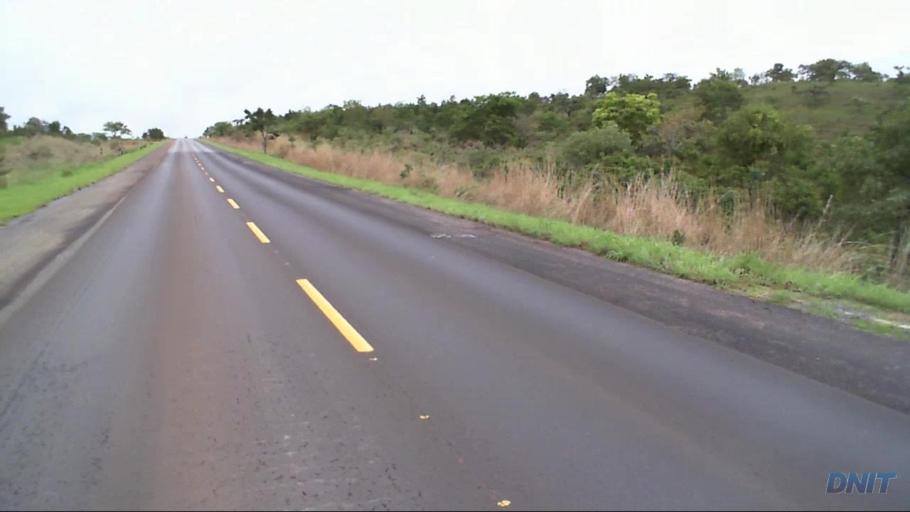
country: BR
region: Goias
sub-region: Padre Bernardo
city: Padre Bernardo
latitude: -15.1969
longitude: -48.4451
